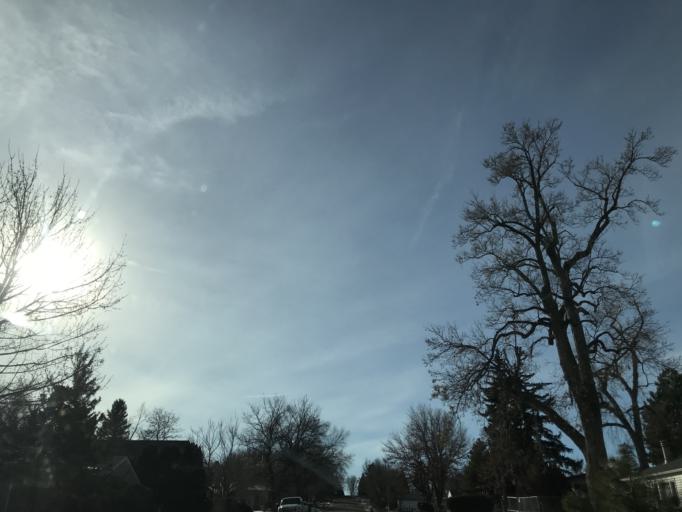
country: US
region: Colorado
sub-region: Arapahoe County
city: Littleton
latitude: 39.6000
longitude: -105.0093
